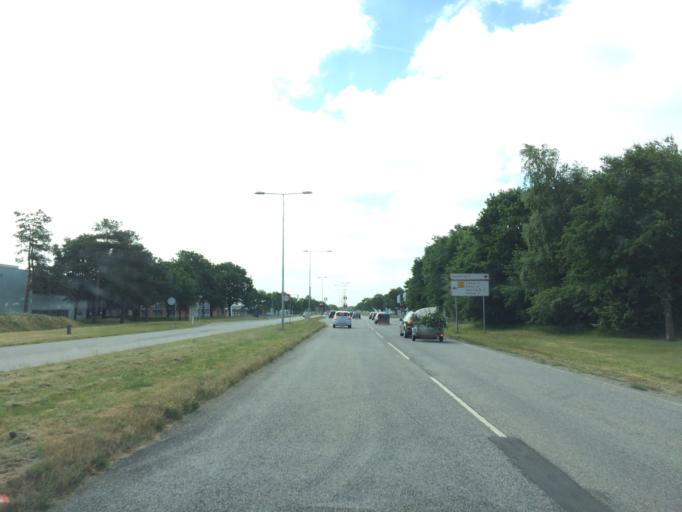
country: DK
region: Central Jutland
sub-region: Herning Kommune
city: Snejbjerg
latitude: 56.1585
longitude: 8.9268
